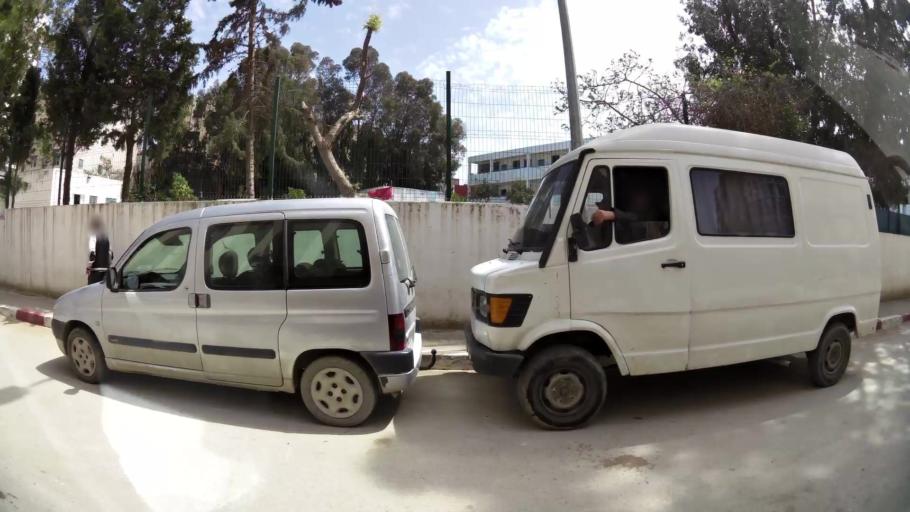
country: MA
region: Tanger-Tetouan
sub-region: Tanger-Assilah
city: Tangier
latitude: 35.7399
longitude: -5.8314
